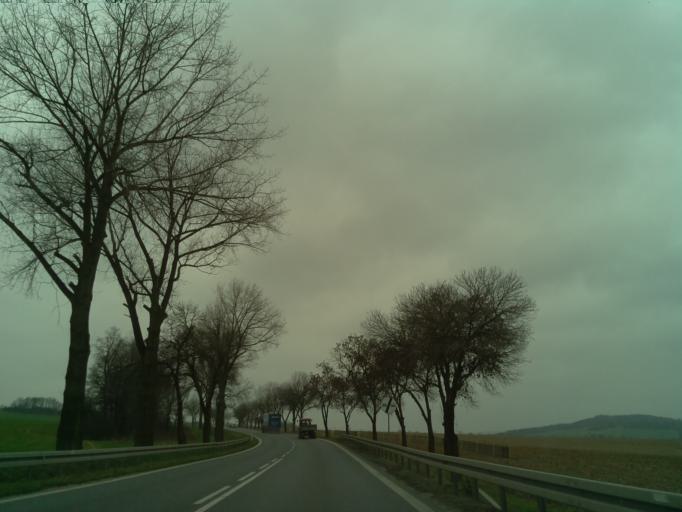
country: PL
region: Lower Silesian Voivodeship
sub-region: Powiat swidnicki
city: Strzegom
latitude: 50.9884
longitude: 16.3996
